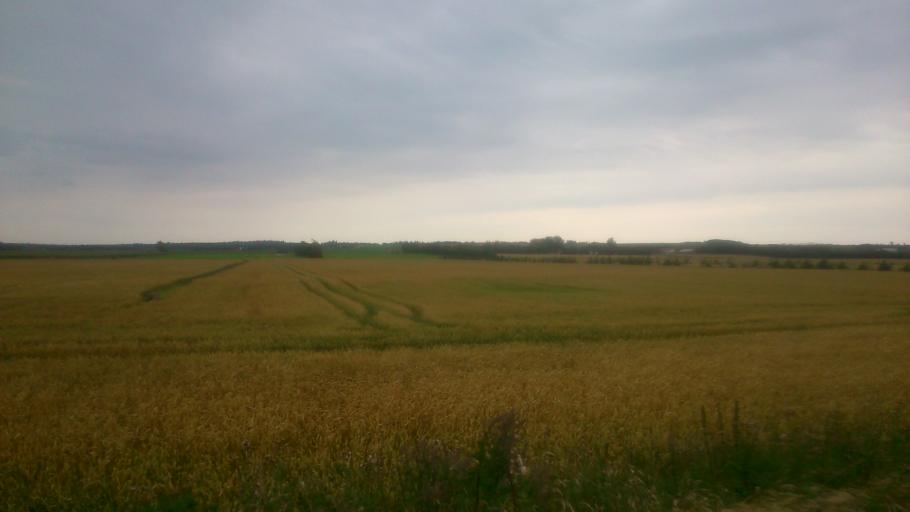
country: DK
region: Central Jutland
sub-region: Ringkobing-Skjern Kommune
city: Skjern
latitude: 55.9146
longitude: 8.4717
